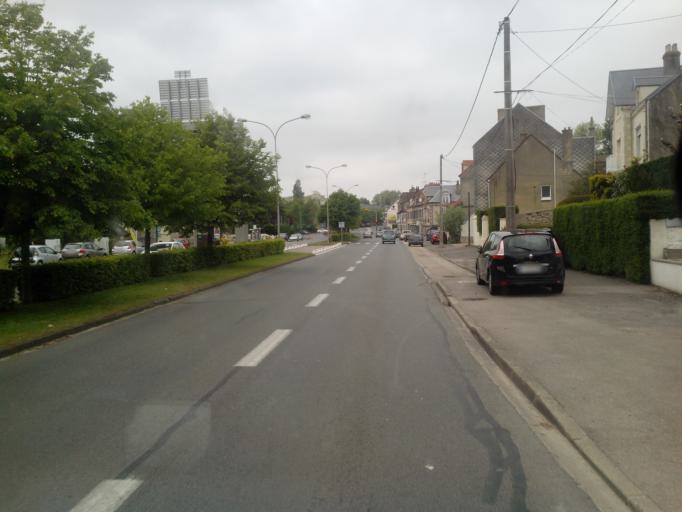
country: FR
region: Nord-Pas-de-Calais
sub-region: Departement du Pas-de-Calais
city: Saint-Etienne-au-Mont
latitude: 50.6843
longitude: 1.6308
